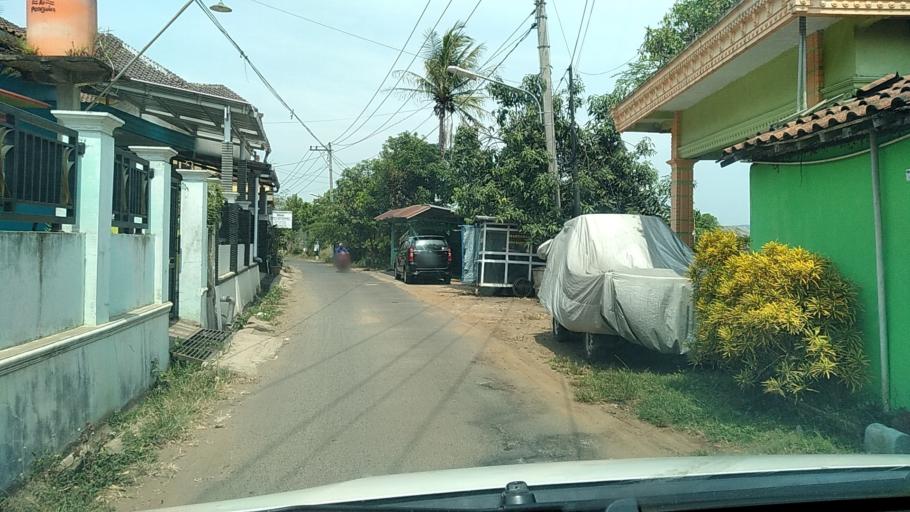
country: ID
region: Central Java
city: Ungaran
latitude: -7.0798
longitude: 110.3089
